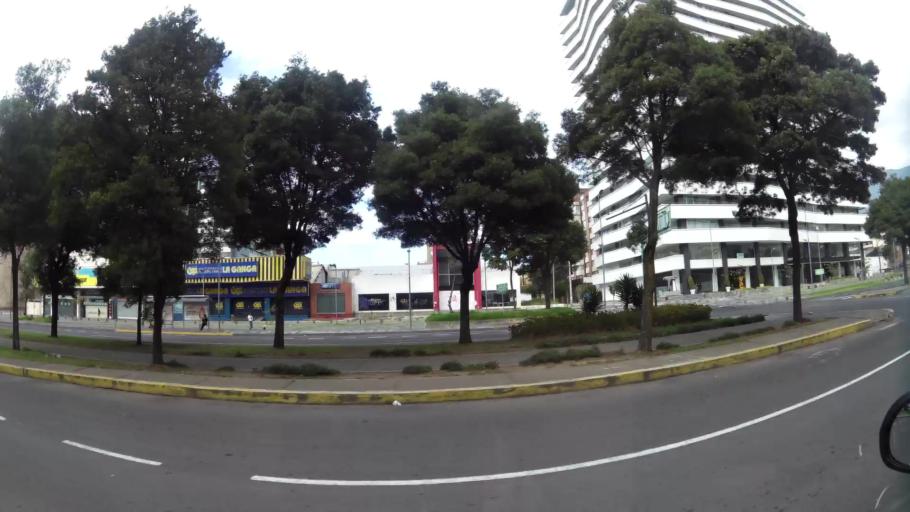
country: EC
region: Pichincha
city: Quito
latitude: -0.1754
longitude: -78.4866
